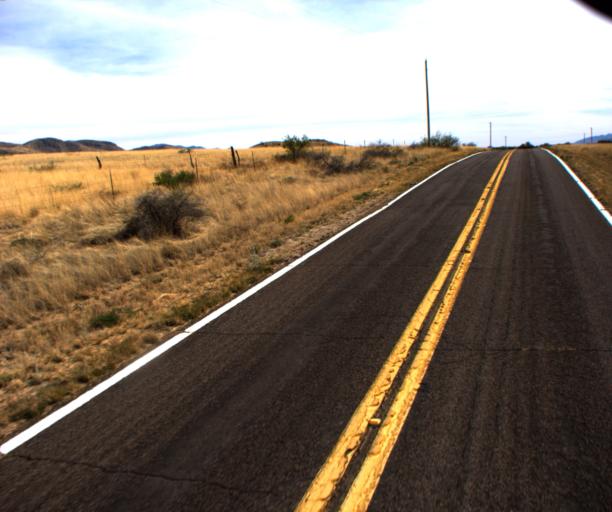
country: US
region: Arizona
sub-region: Cochise County
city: Willcox
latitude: 31.9562
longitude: -109.4772
